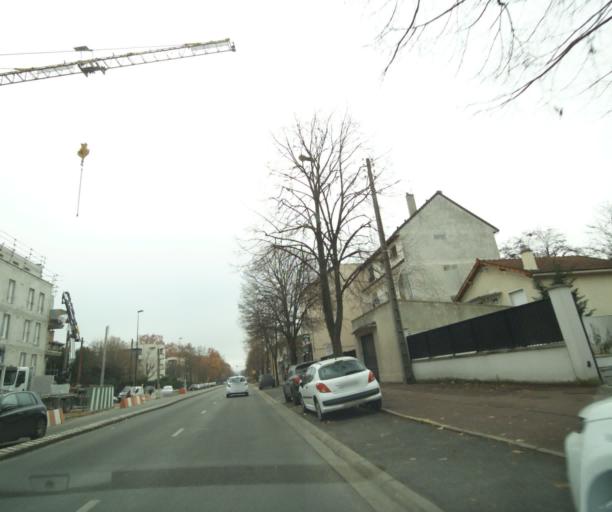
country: FR
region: Ile-de-France
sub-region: Departement de Seine-Saint-Denis
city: Livry-Gargan
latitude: 48.9222
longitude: 2.5246
